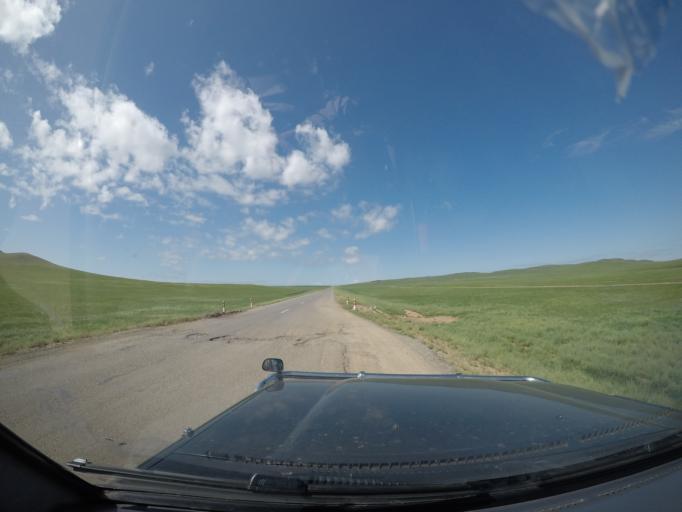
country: MN
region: Suhbaatar
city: Hanhohiy
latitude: 47.3843
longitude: 111.8542
